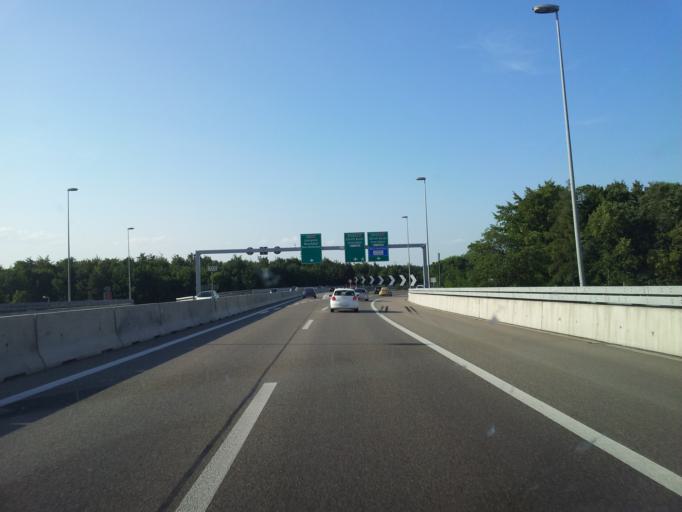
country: CH
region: Bern
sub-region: Bern-Mittelland District
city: Koniz
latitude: 46.9488
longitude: 7.4068
